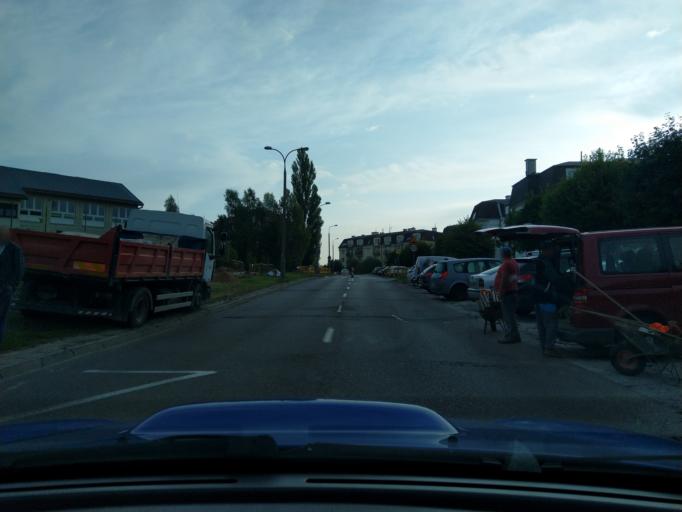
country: PL
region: Warmian-Masurian Voivodeship
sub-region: Olsztyn
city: Kortowo
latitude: 53.7586
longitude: 20.4699
